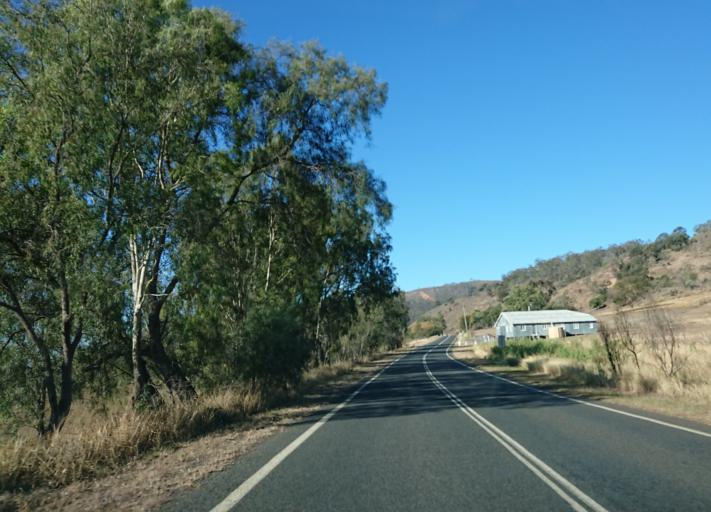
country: AU
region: Queensland
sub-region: Toowoomba
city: Rangeville
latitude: -27.7199
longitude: 152.1179
